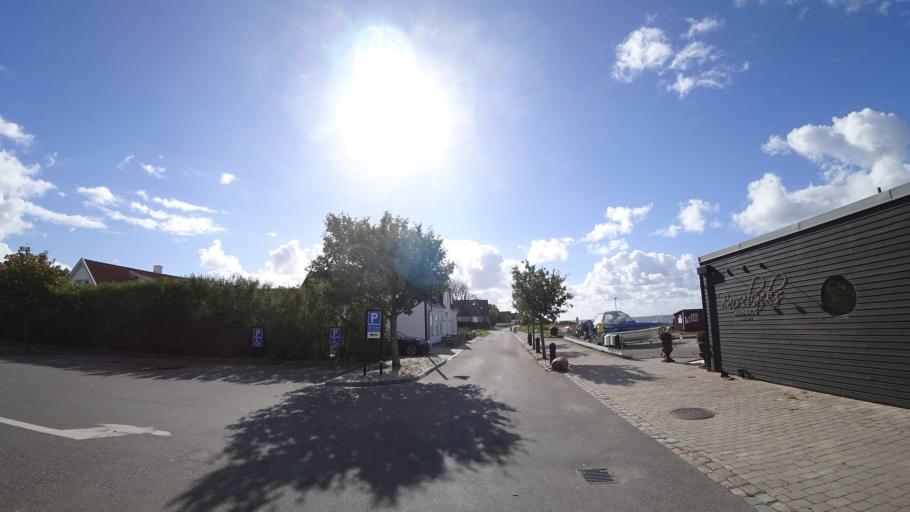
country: SE
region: Skane
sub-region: Kavlinge Kommun
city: Hofterup
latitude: 55.7559
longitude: 12.9053
